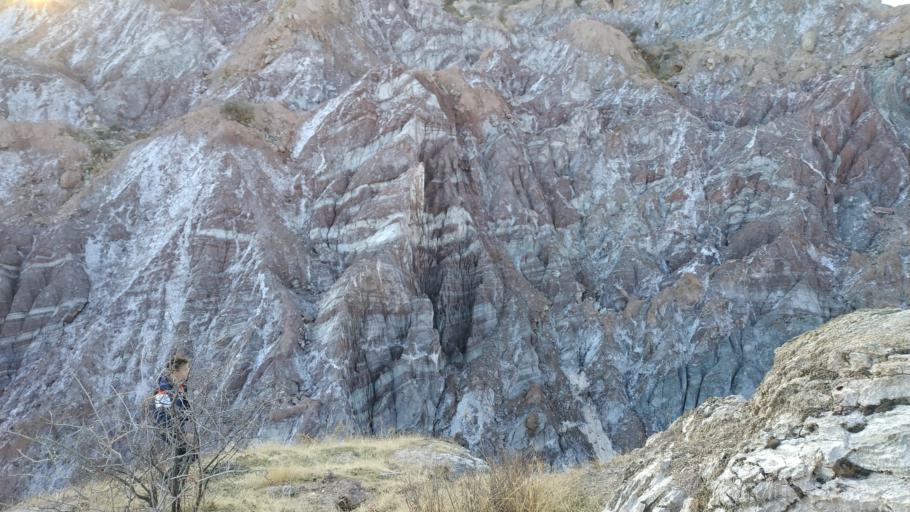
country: TJ
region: Khatlon
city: Moskva
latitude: 37.7280
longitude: 69.6516
